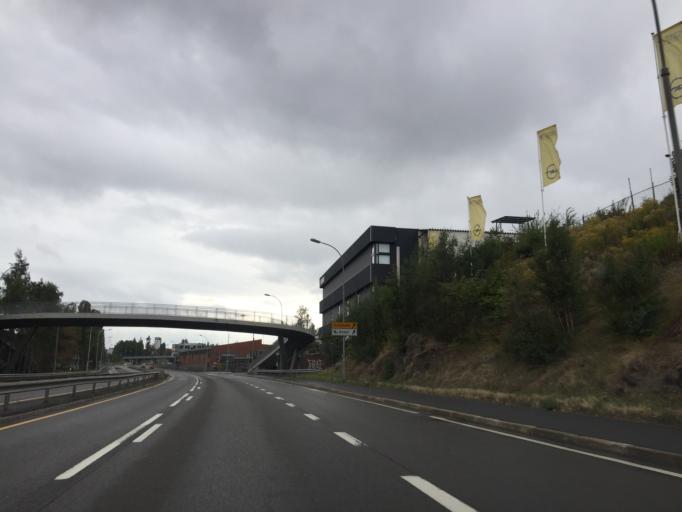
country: NO
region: Oslo
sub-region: Oslo
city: Oslo
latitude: 59.9369
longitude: 10.8346
